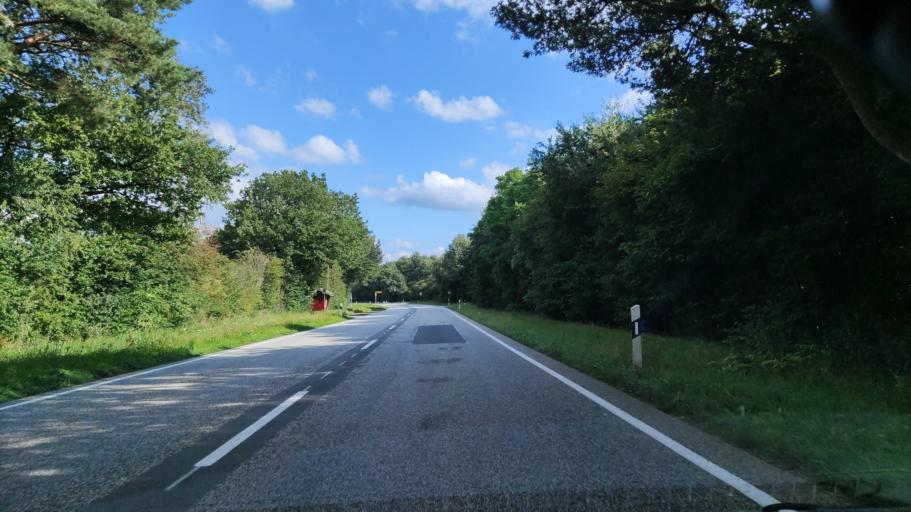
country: DE
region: Schleswig-Holstein
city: Brammer
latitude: 54.2173
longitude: 9.7217
